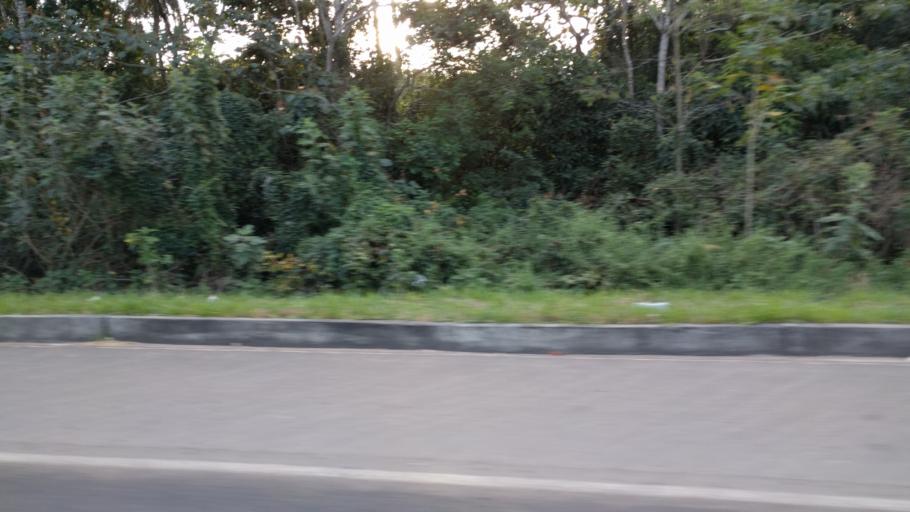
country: BO
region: Santa Cruz
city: Buena Vista
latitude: -17.4170
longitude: -63.6194
